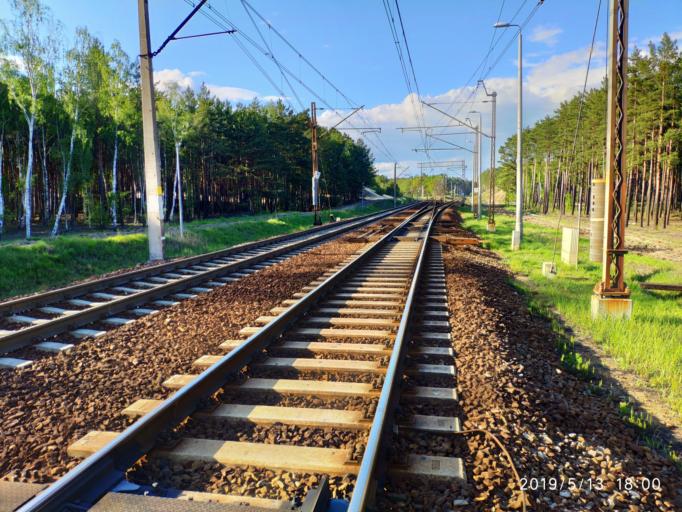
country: PL
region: Lubusz
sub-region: Powiat zielonogorski
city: Czerwiensk
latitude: 52.0041
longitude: 15.4341
